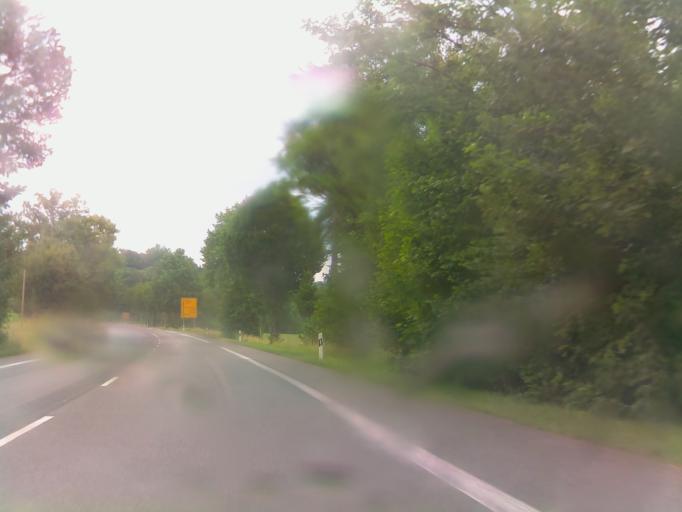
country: DE
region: North Rhine-Westphalia
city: Brakel
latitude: 51.7511
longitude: 9.1770
